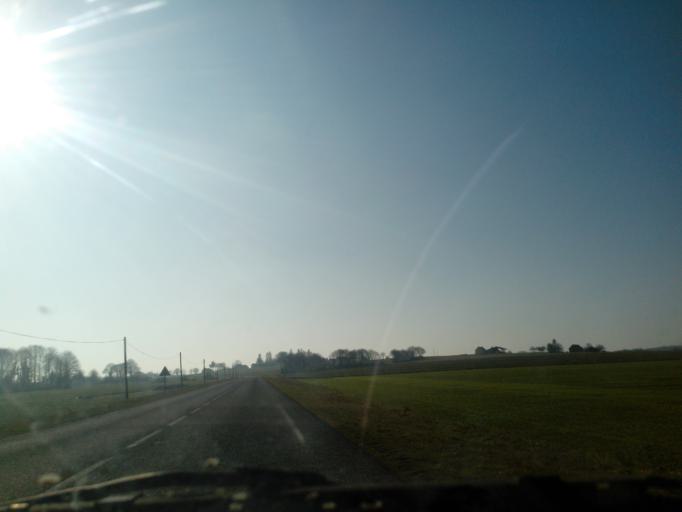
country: FR
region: Brittany
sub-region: Departement des Cotes-d'Armor
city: Merdrignac
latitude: 48.1671
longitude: -2.4386
